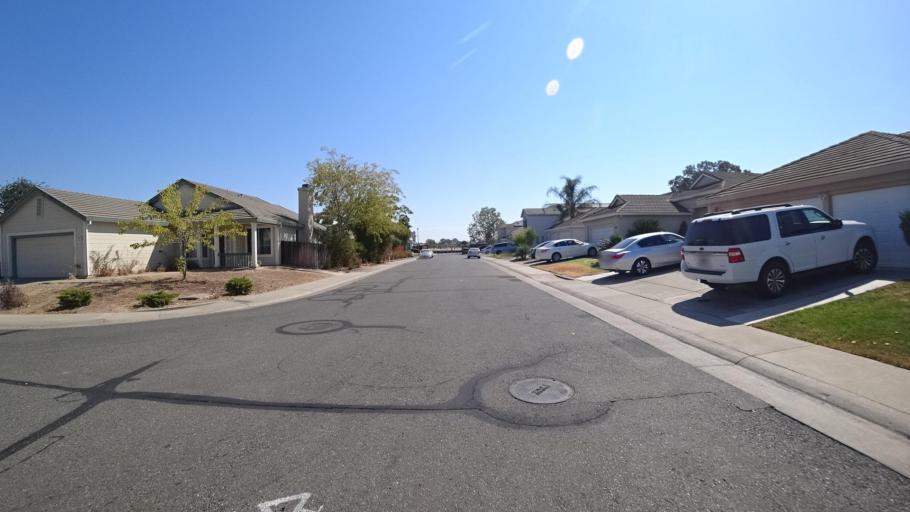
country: US
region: California
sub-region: Sacramento County
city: Vineyard
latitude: 38.4494
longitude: -121.3830
